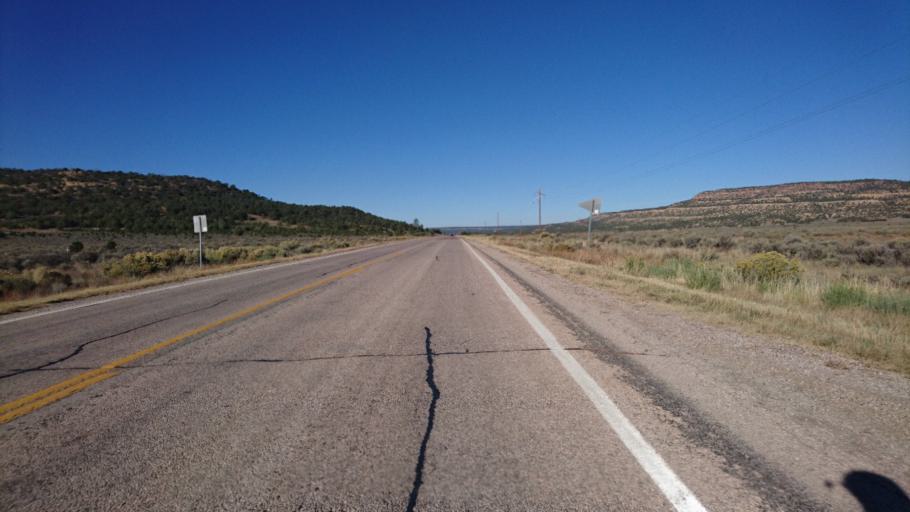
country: US
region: New Mexico
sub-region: McKinley County
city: Black Rock
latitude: 35.1205
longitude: -108.6236
